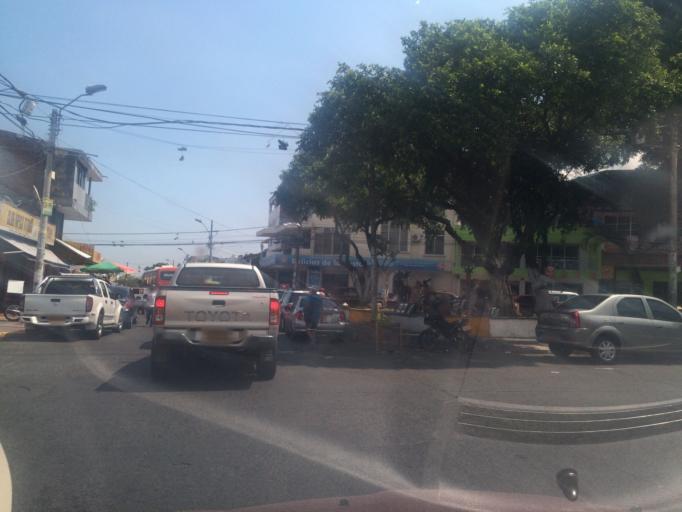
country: CO
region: Valle del Cauca
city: Cali
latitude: 3.4357
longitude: -76.5358
